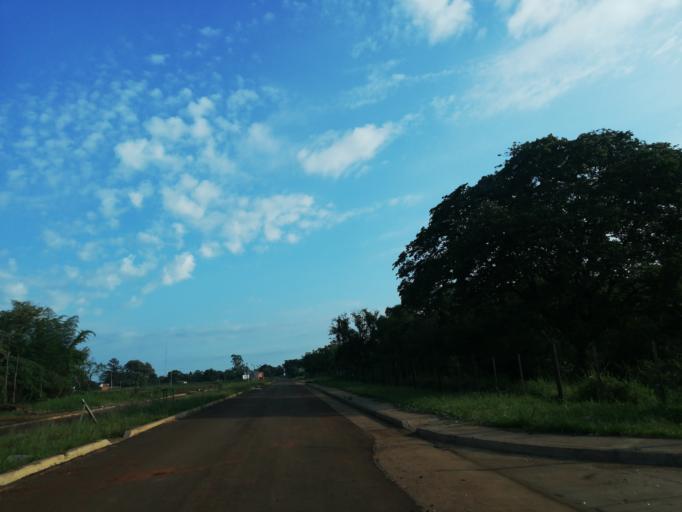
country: AR
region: Misiones
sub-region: Departamento de Capital
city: Posadas
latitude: -27.3943
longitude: -55.9241
